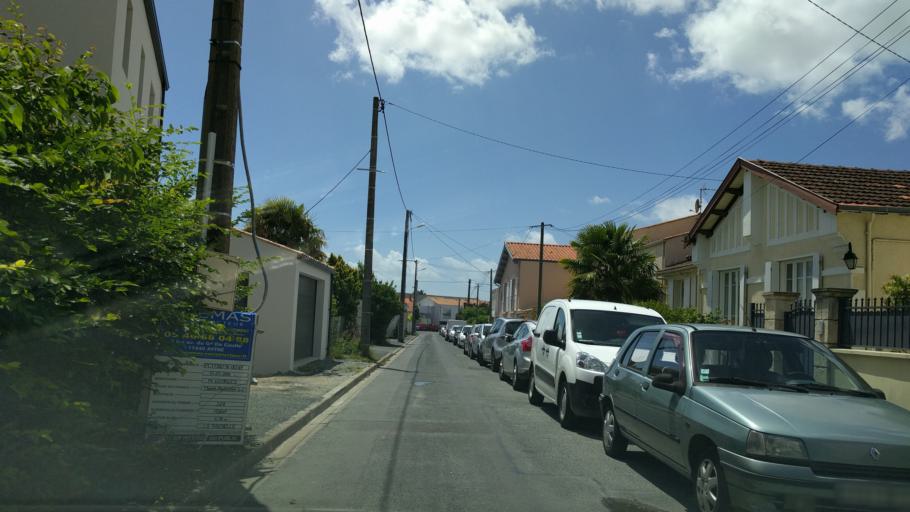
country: FR
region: Poitou-Charentes
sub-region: Departement de la Charente-Maritime
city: La Rochelle
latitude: 46.1622
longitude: -1.1362
